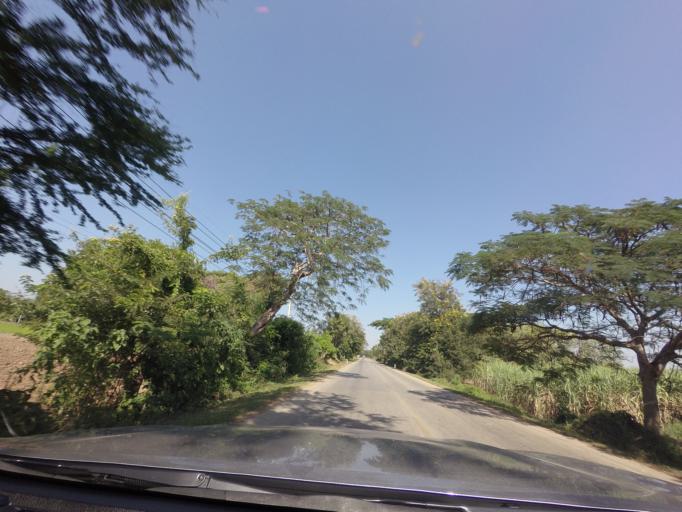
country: TH
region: Sukhothai
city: Sawankhalok
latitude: 17.3277
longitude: 99.8222
